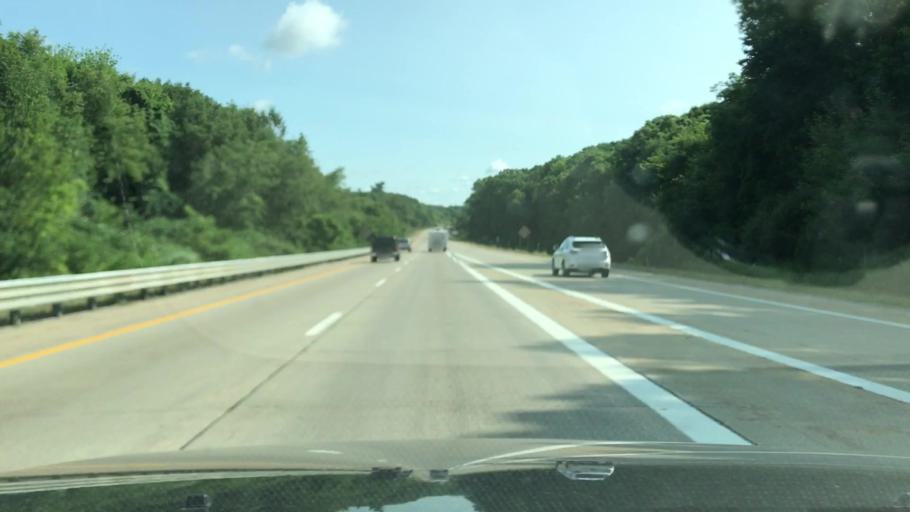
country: US
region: Michigan
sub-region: Kent County
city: Northview
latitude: 43.0926
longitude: -85.6289
